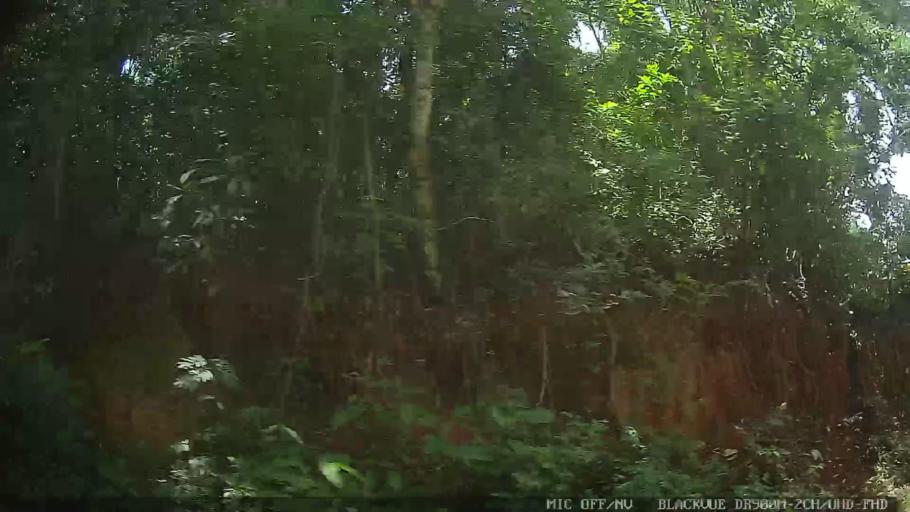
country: BR
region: Sao Paulo
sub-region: Santa Isabel
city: Santa Isabel
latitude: -23.3452
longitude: -46.1941
